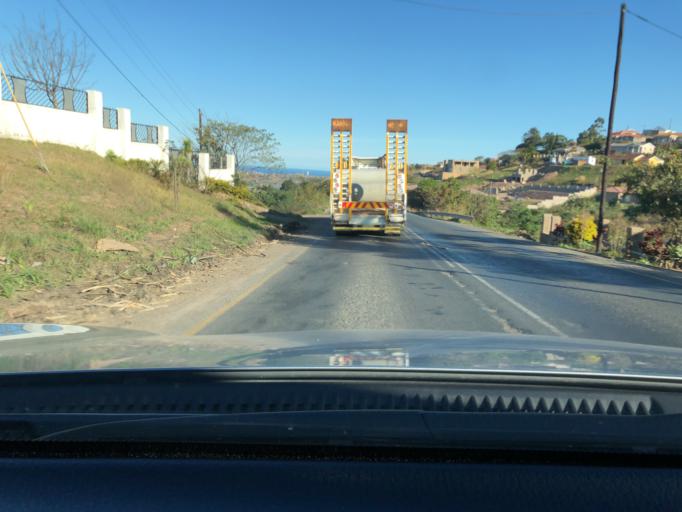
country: ZA
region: KwaZulu-Natal
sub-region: eThekwini Metropolitan Municipality
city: Umkomaas
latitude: -30.0180
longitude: 30.8088
